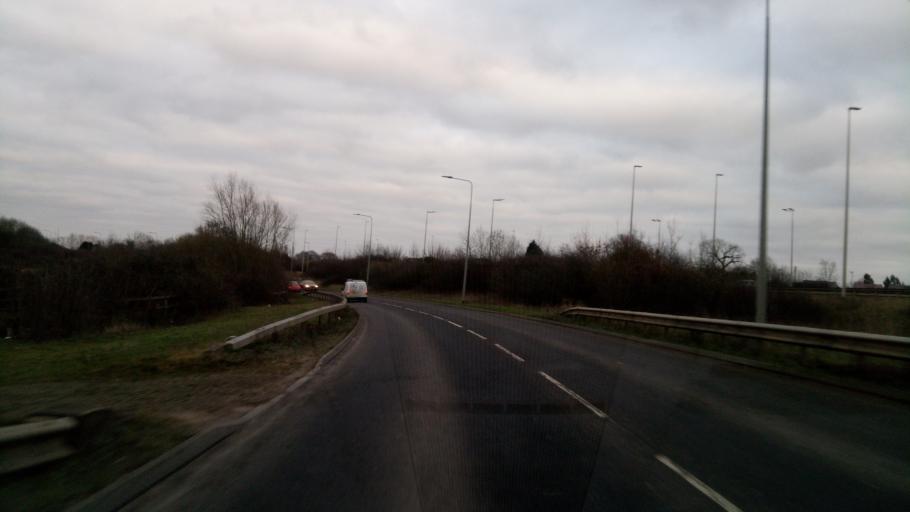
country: GB
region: England
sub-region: Peterborough
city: Peterborough
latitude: 52.5494
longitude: -0.2348
